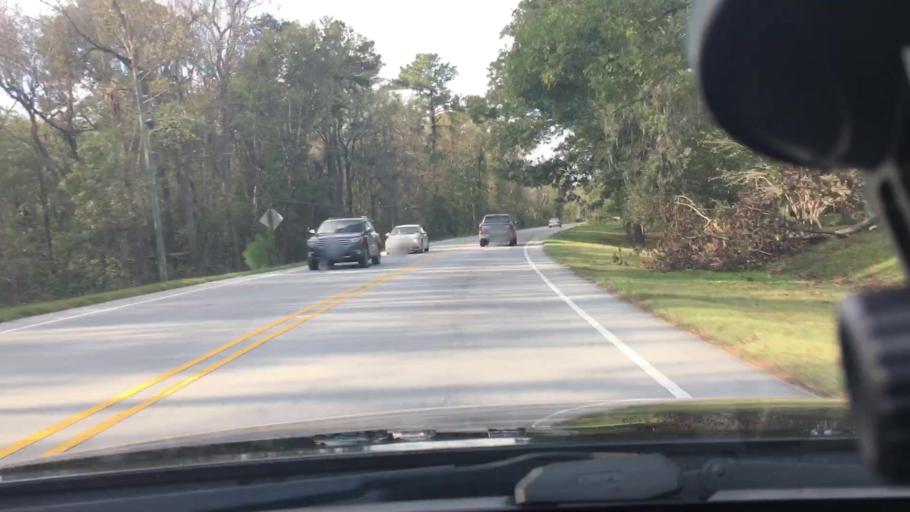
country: US
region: North Carolina
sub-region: Craven County
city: Vanceboro
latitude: 35.2295
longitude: -77.0721
